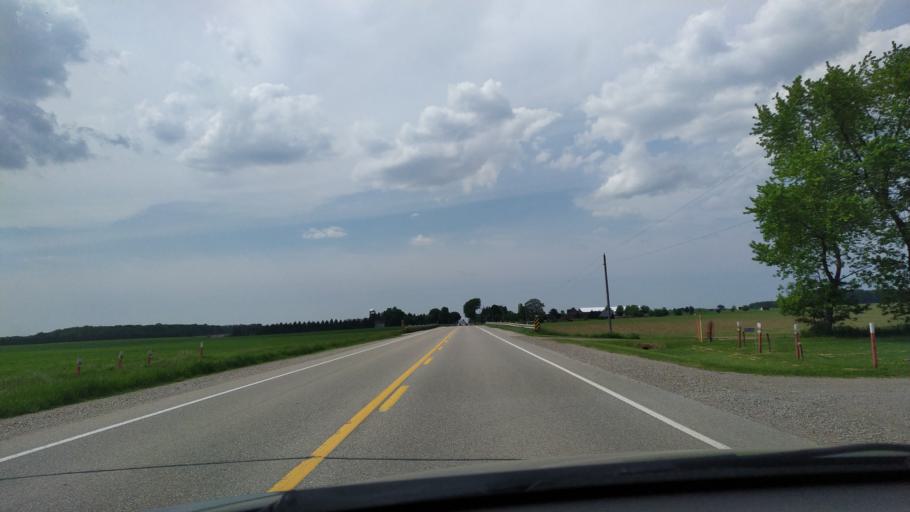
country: CA
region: Ontario
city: Dorchester
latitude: 43.1735
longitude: -81.0477
